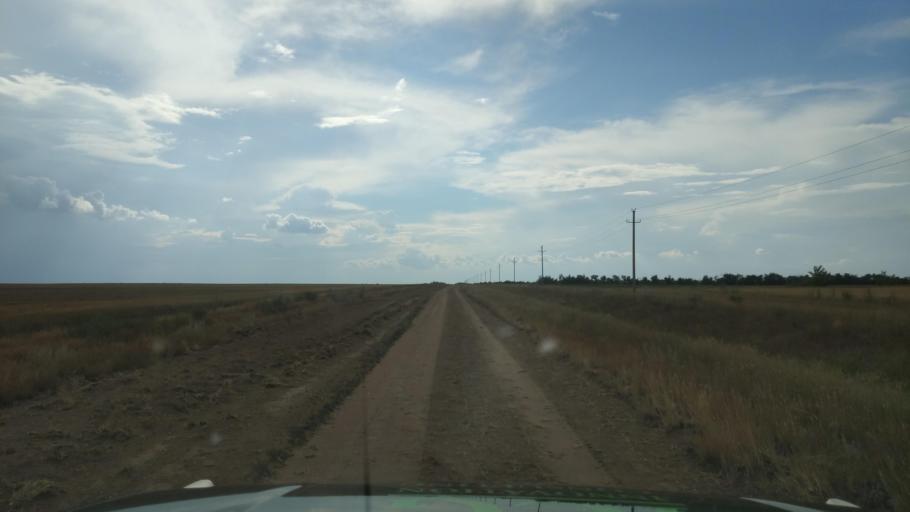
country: KZ
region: Pavlodar
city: Pavlodar
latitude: 52.5124
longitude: 77.5189
